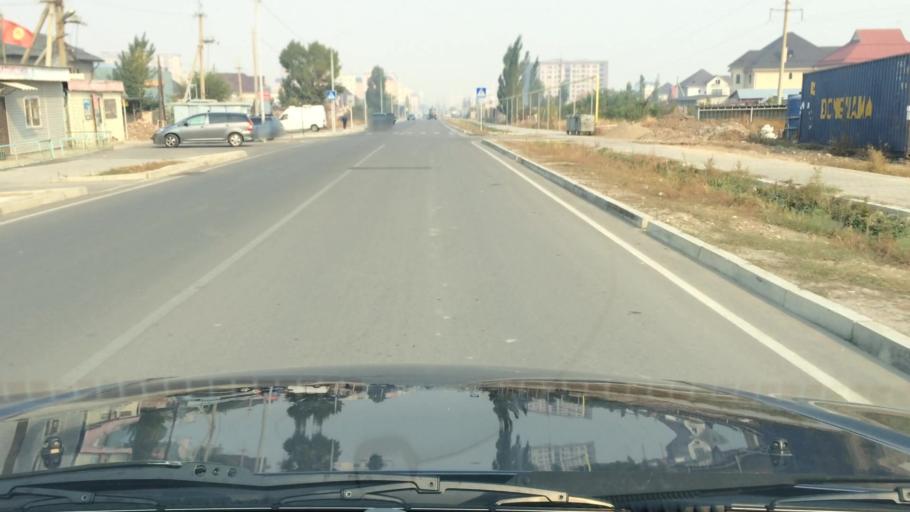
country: KG
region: Chuy
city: Bishkek
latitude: 42.8246
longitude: 74.5698
